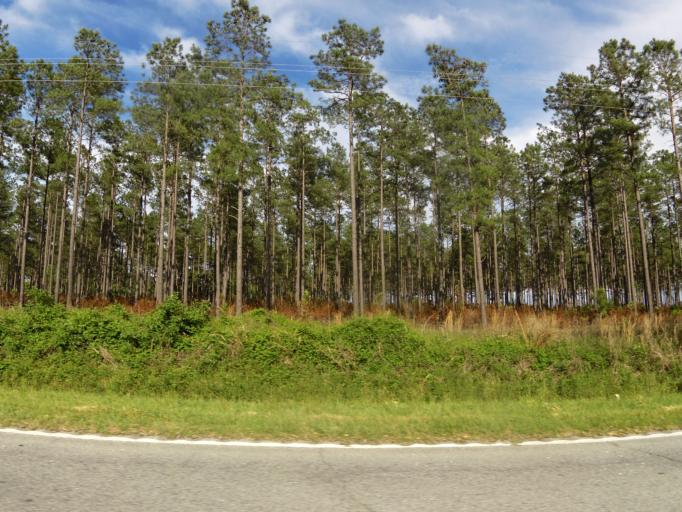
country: US
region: South Carolina
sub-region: Allendale County
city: Fairfax
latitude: 32.8935
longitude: -81.2380
